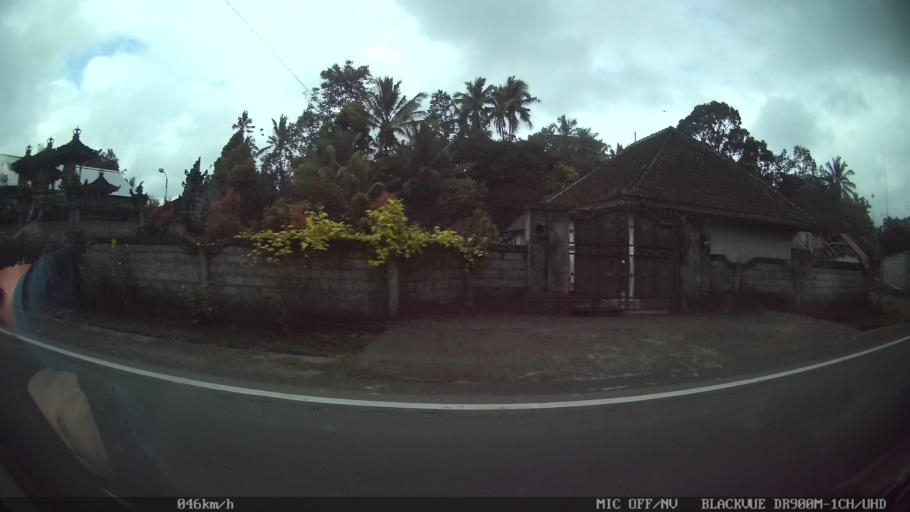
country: ID
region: Bali
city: Banjar Kubu
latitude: -8.4284
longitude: 115.4277
